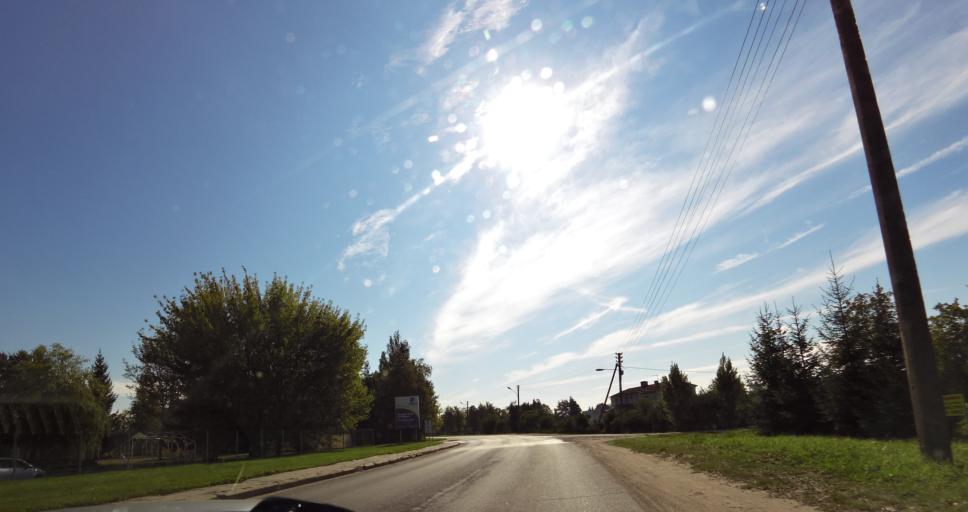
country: LT
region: Panevezys
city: Pasvalys
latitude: 56.0670
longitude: 24.3869
